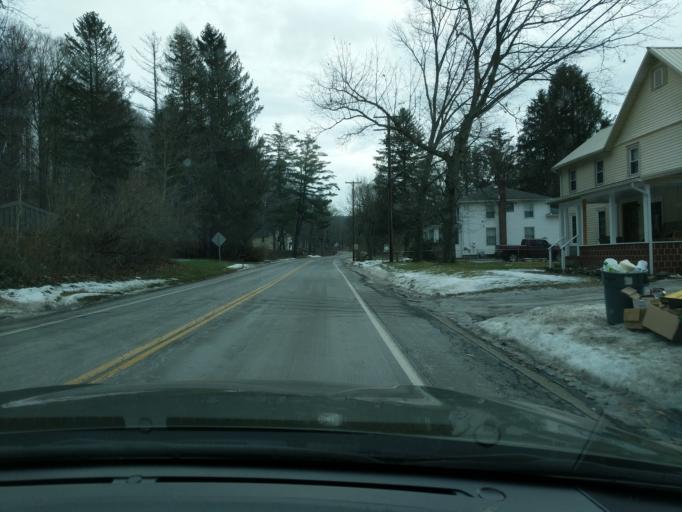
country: US
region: New York
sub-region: Tompkins County
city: East Ithaca
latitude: 42.3878
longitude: -76.4069
